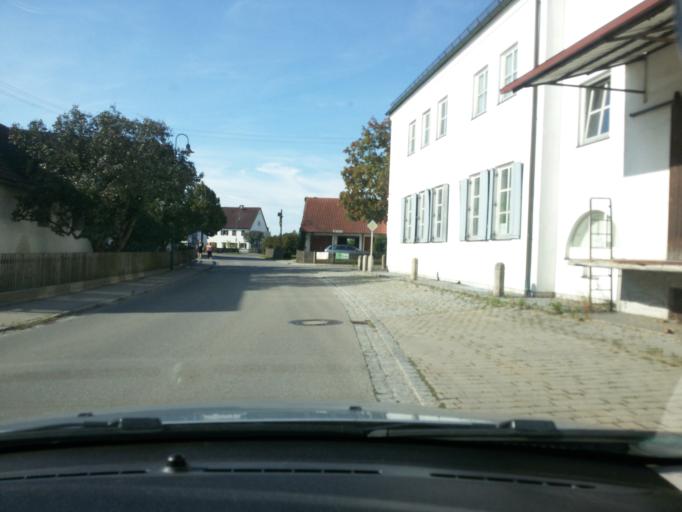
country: DE
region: Bavaria
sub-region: Swabia
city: Kutzenhausen
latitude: 48.3413
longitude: 10.6942
